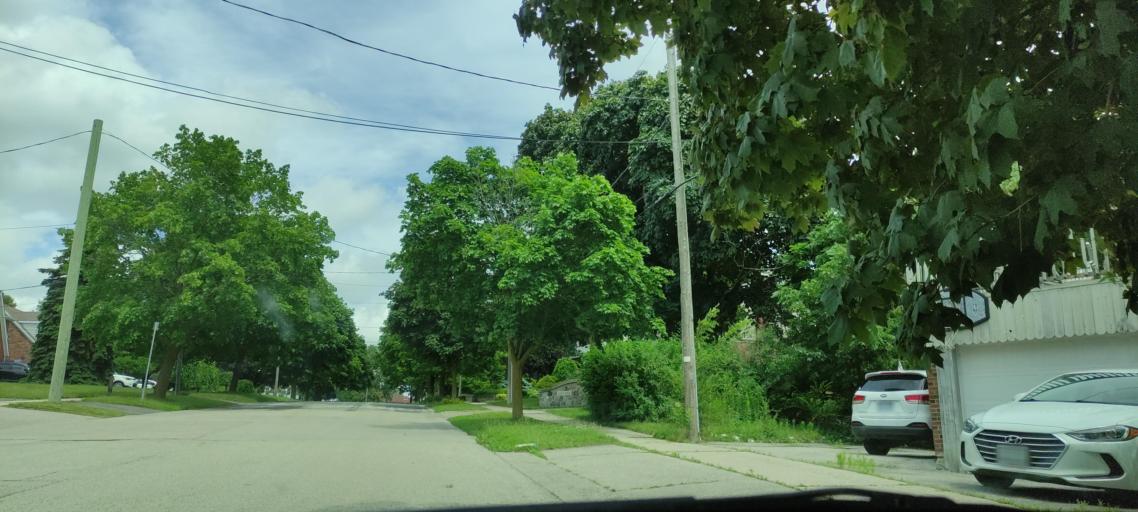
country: CA
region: Ontario
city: Kitchener
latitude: 43.4412
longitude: -80.4609
